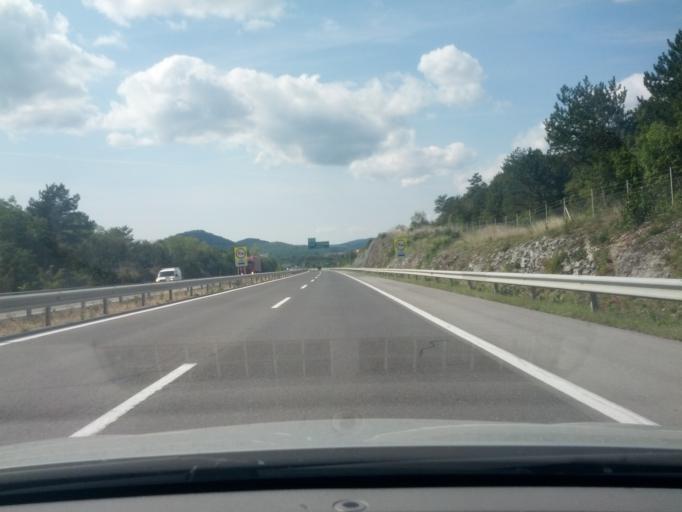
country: SI
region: Sezana
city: Sezana
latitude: 45.7126
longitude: 13.9083
